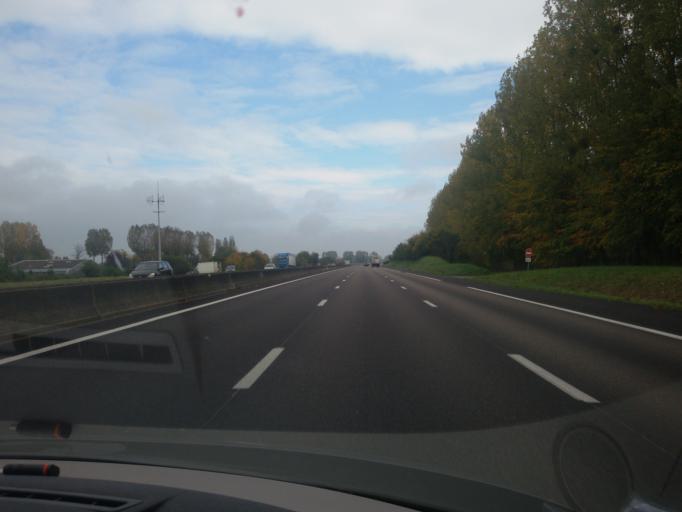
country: FR
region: Haute-Normandie
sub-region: Departement de l'Eure
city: Hauville
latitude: 49.3698
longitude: 0.7542
